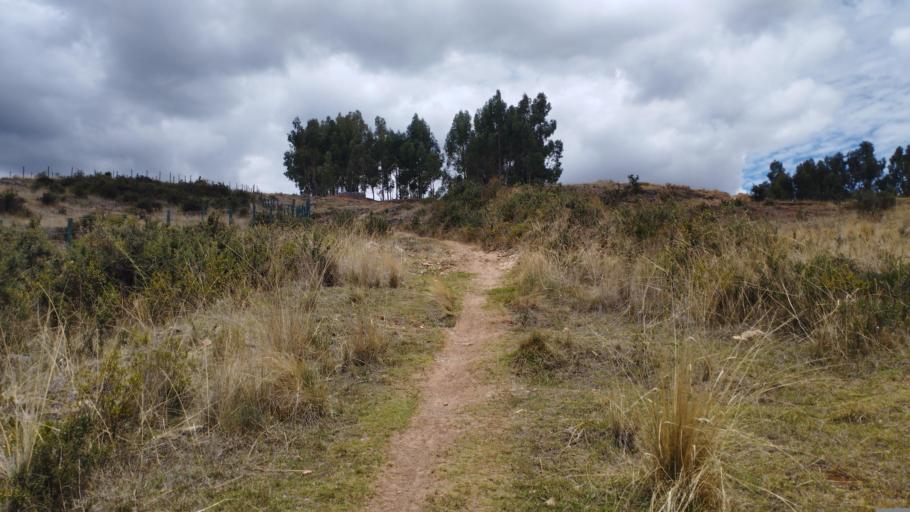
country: PE
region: Cusco
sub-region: Provincia de Cusco
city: Cusco
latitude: -13.5156
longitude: -71.9421
